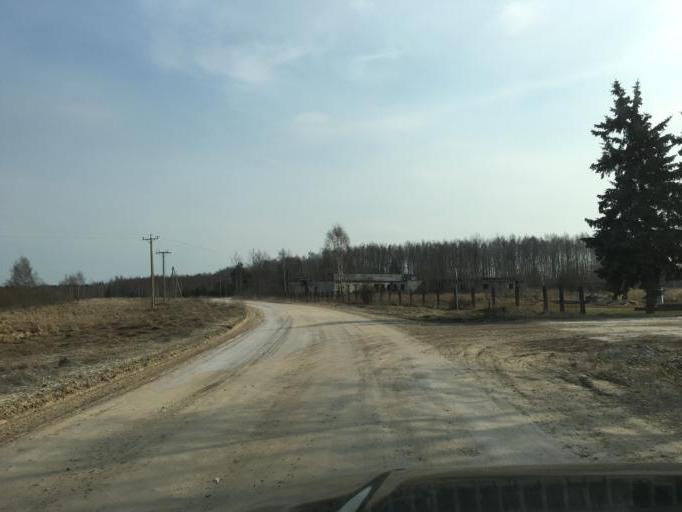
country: LV
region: Olaine
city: Olaine
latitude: 56.7946
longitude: 23.9824
